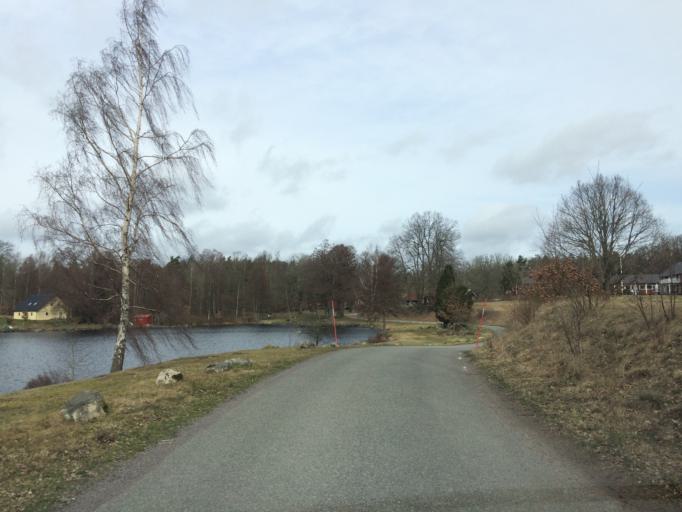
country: SE
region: Skane
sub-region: Ostra Goinge Kommun
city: Sibbhult
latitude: 56.2784
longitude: 14.3038
